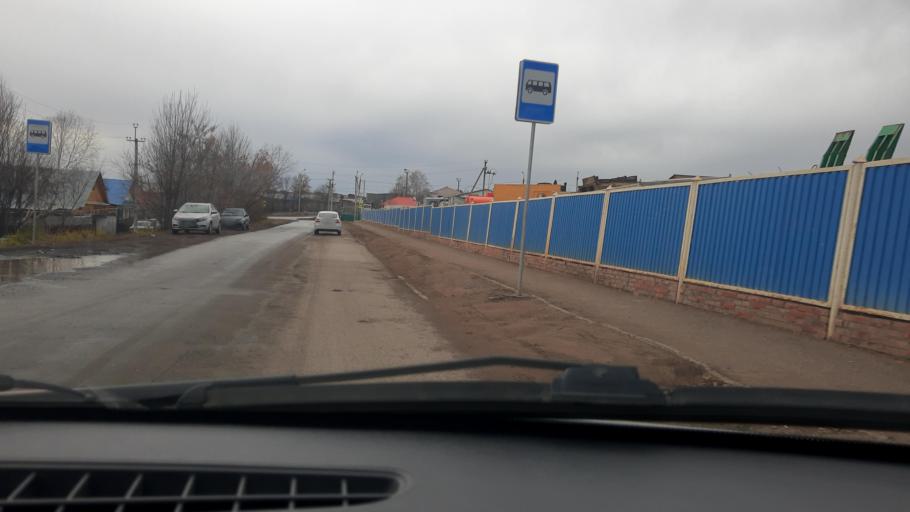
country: RU
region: Bashkortostan
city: Avdon
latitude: 54.6914
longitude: 55.8085
